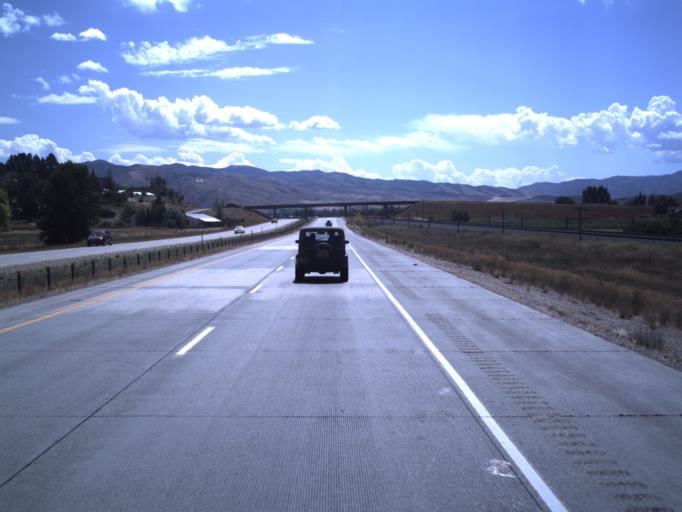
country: US
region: Utah
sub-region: Morgan County
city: Morgan
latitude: 41.0702
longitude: -111.7155
